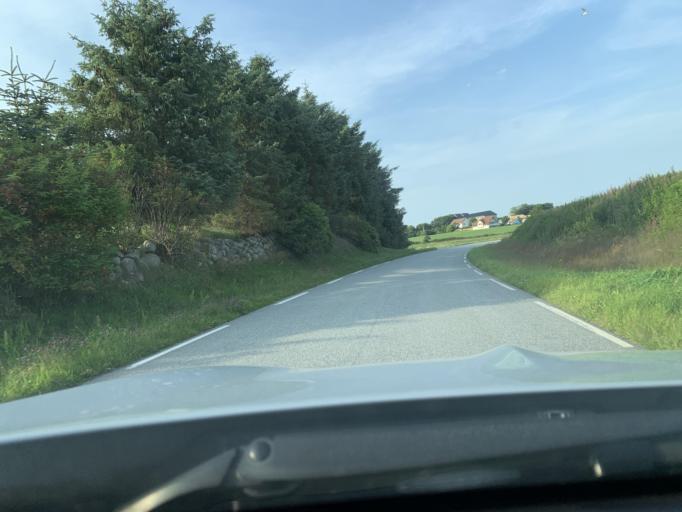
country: NO
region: Rogaland
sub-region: Time
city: Bryne
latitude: 58.7300
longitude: 5.5873
